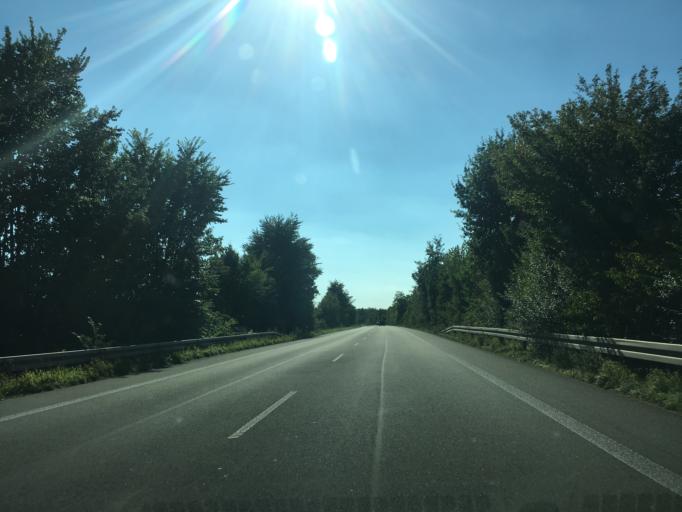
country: DE
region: North Rhine-Westphalia
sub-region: Regierungsbezirk Detmold
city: Rheda-Wiedenbruck
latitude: 51.8762
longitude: 8.2751
